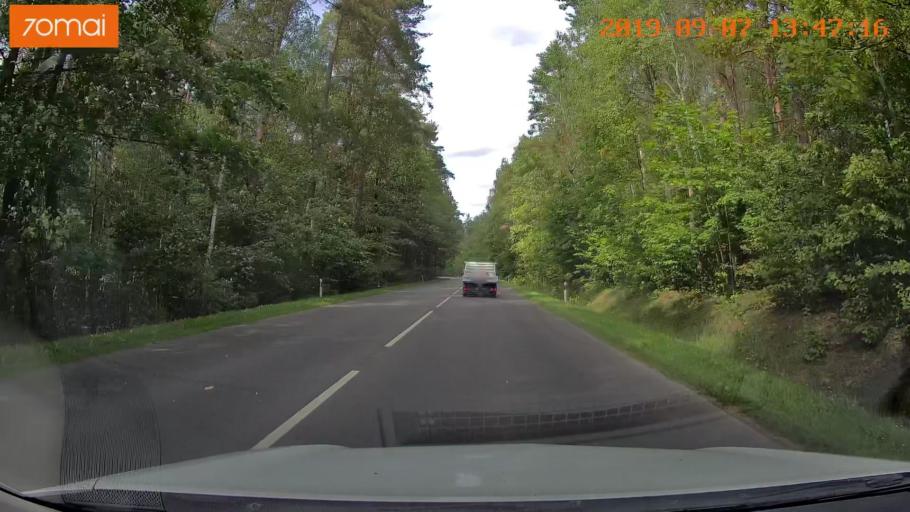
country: LT
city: Baltoji Voke
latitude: 54.5961
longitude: 25.2166
